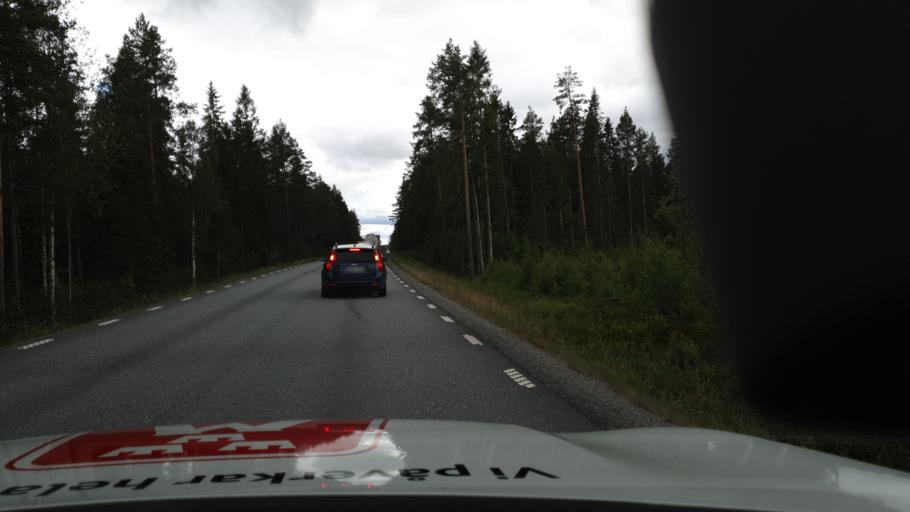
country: SE
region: Vaesterbotten
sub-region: Skelleftea Kommun
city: Viken
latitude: 64.6183
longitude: 20.9562
